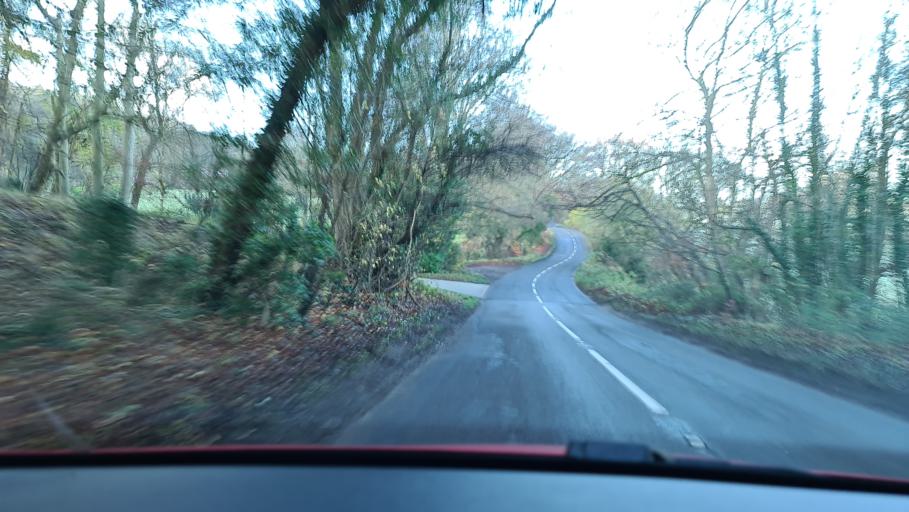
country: GB
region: England
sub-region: Buckinghamshire
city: Wendover
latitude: 51.7572
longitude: -0.7675
